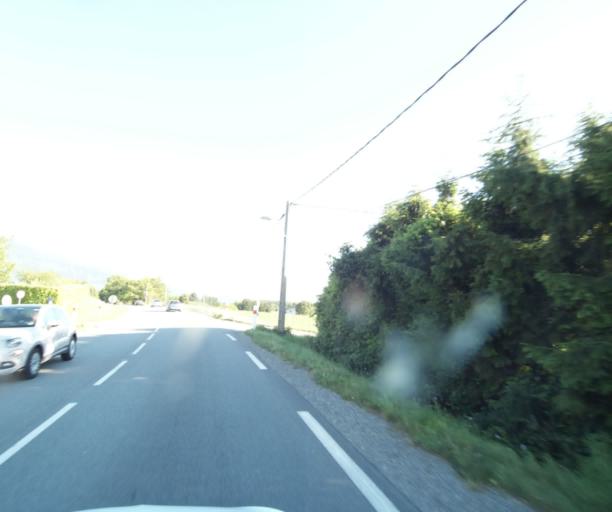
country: FR
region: Rhone-Alpes
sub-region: Departement de la Haute-Savoie
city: Loisin
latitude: 46.2829
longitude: 6.3094
